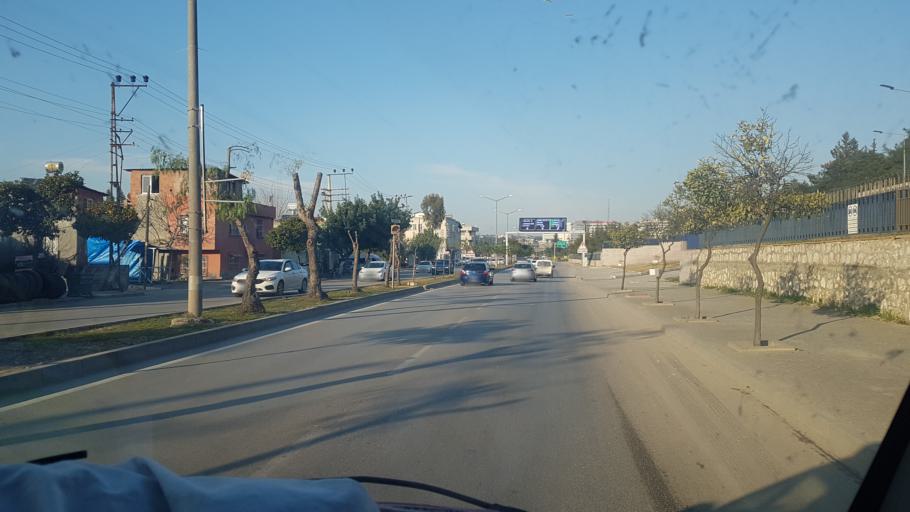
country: TR
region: Adana
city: Adana
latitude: 37.0188
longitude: 35.3412
